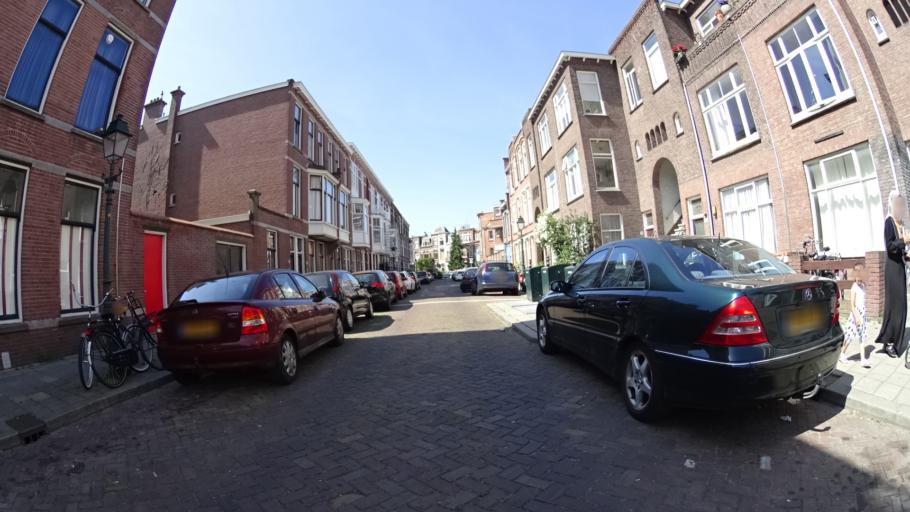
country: NL
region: South Holland
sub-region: Gemeente Den Haag
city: The Hague
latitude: 52.0746
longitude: 4.2773
